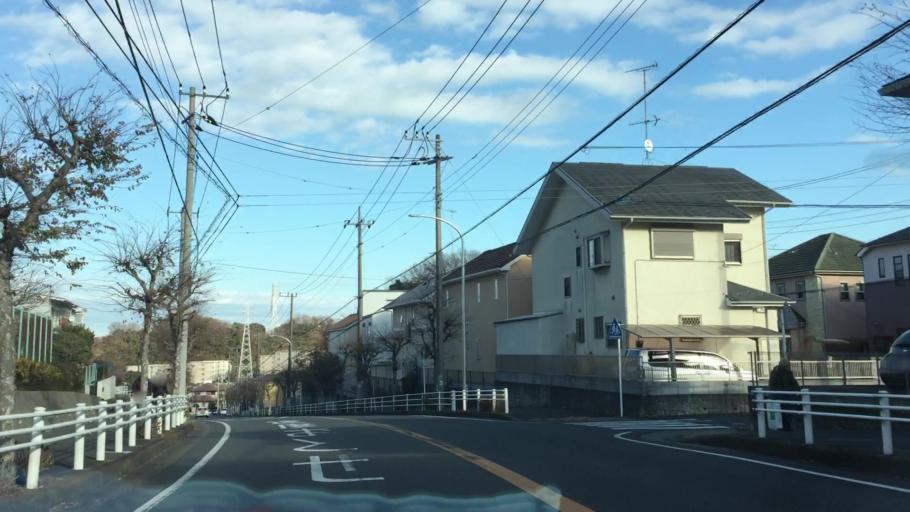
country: JP
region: Kanagawa
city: Zushi
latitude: 35.3383
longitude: 139.6063
